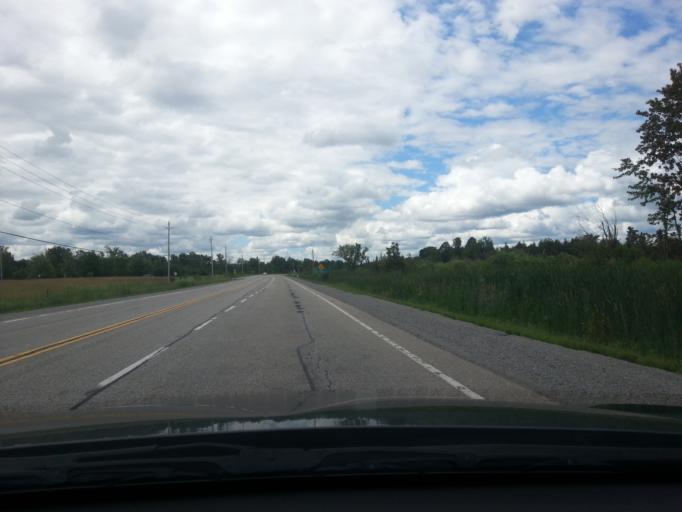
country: CA
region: Ontario
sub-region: Lanark County
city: Smiths Falls
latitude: 44.7505
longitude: -76.1301
